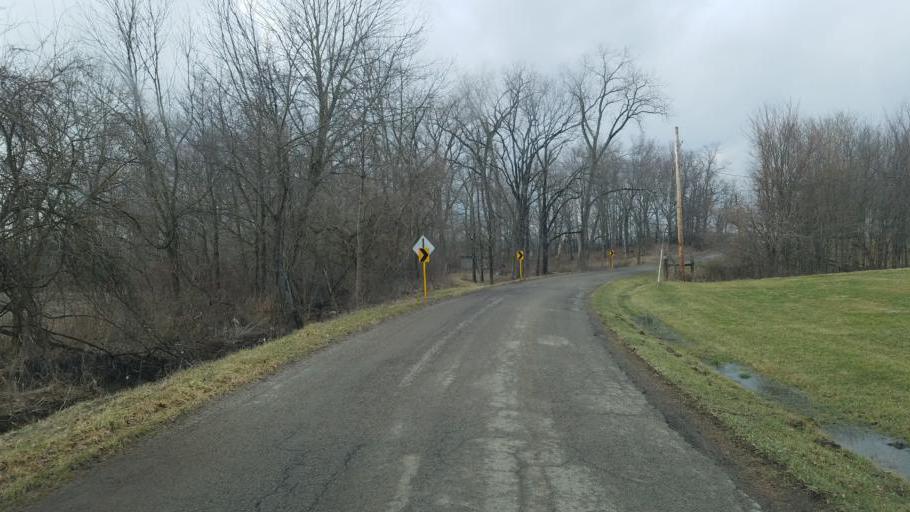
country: US
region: Ohio
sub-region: Knox County
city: Fredericktown
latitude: 40.4867
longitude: -82.6834
